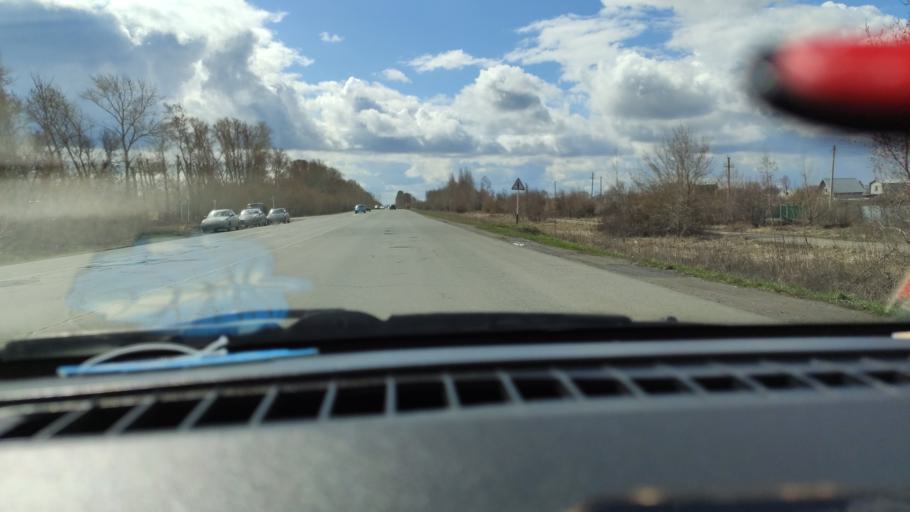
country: RU
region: Samara
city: Tol'yatti
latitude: 53.6983
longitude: 49.4201
